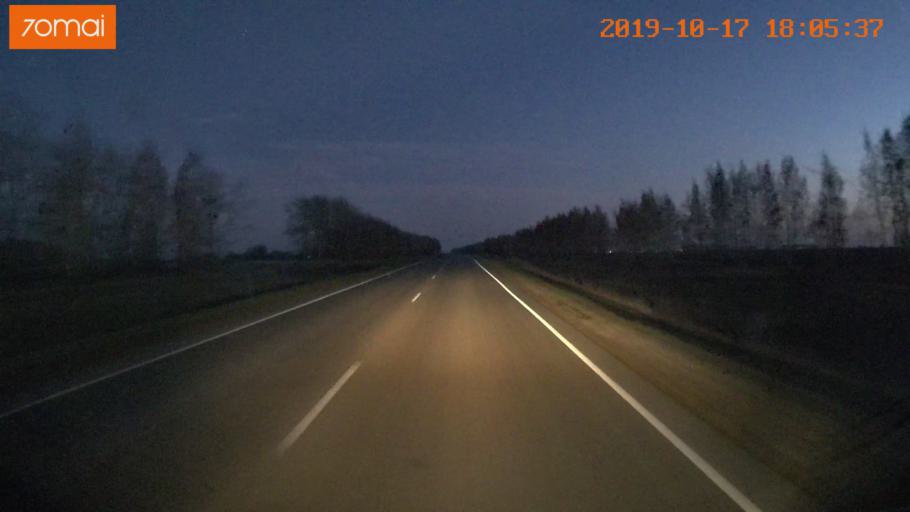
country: RU
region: Tula
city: Kurkino
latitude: 53.4636
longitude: 38.6461
